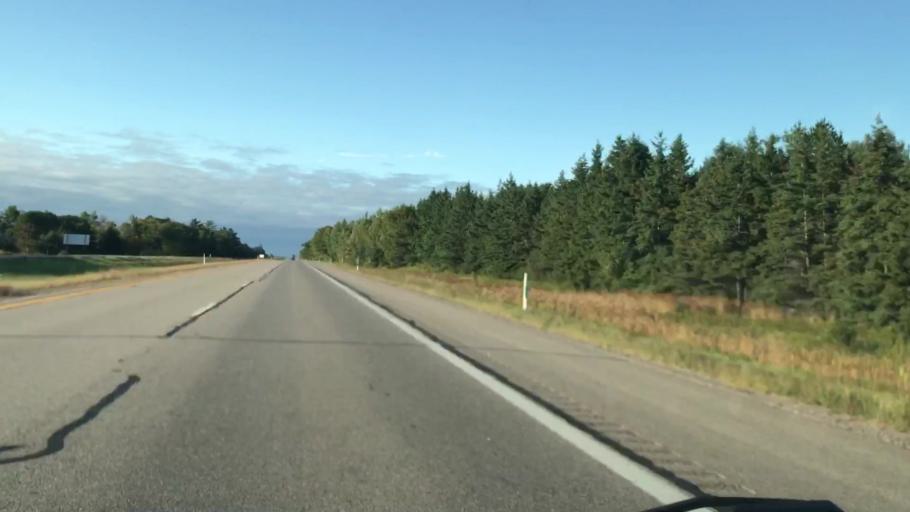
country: US
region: Michigan
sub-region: Chippewa County
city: Sault Ste. Marie
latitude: 46.4387
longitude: -84.3881
